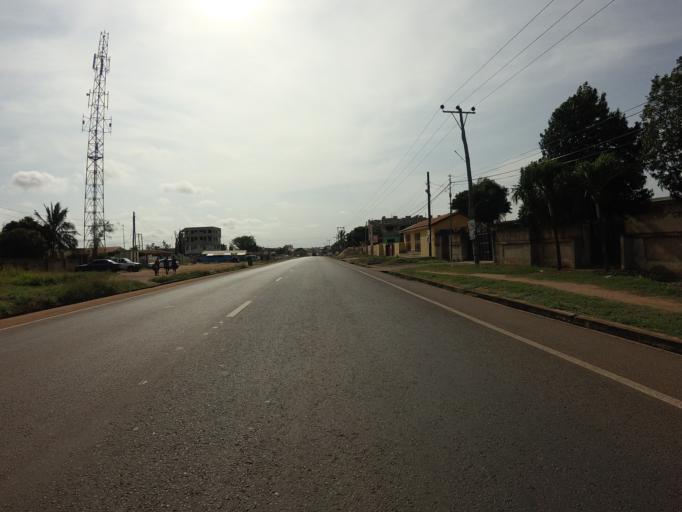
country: GH
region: Greater Accra
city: Nungua
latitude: 5.6450
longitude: -0.0958
